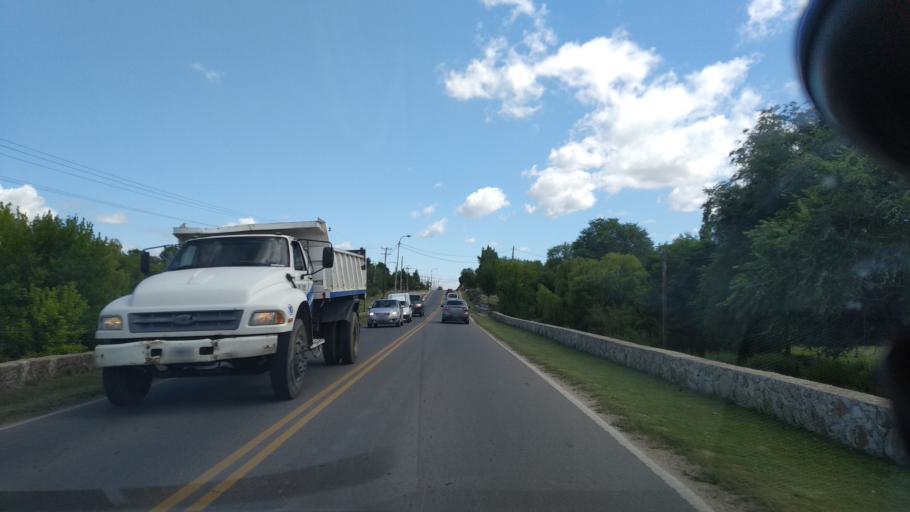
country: AR
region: Cordoba
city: Mina Clavero
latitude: -31.7610
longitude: -65.0013
